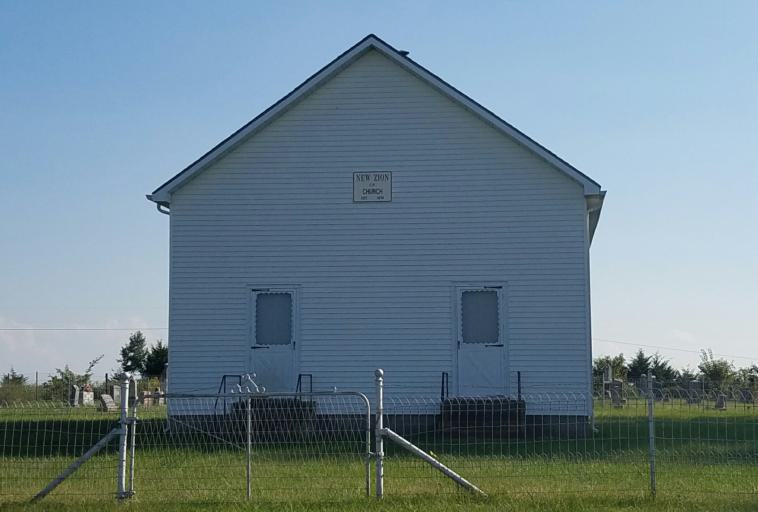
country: US
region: Missouri
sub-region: Moniteau County
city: California
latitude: 38.7108
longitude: -92.6425
